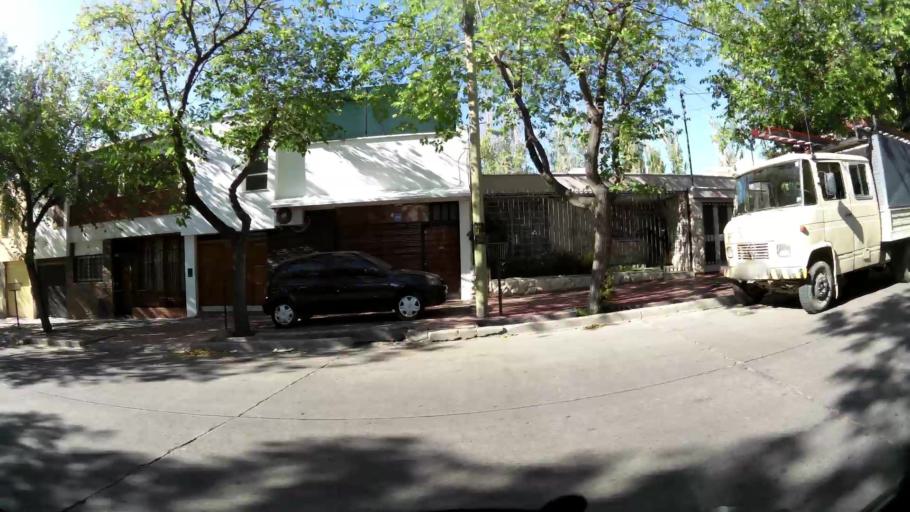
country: AR
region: Mendoza
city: Las Heras
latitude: -32.8707
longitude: -68.8577
